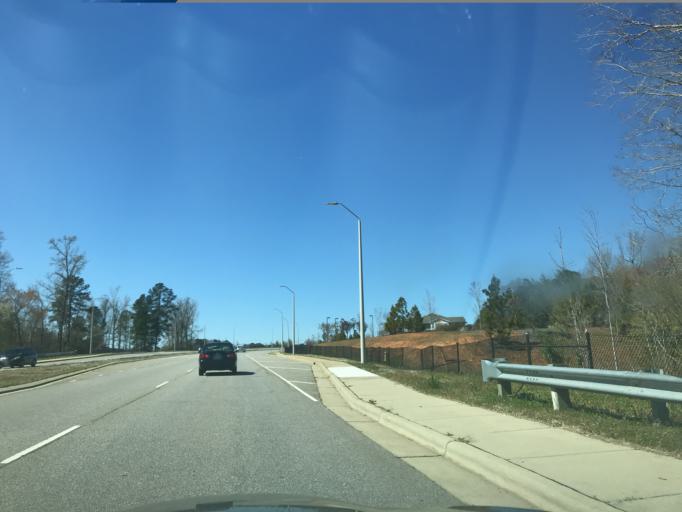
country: US
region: North Carolina
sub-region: Wake County
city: Garner
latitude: 35.6866
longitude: -78.5982
